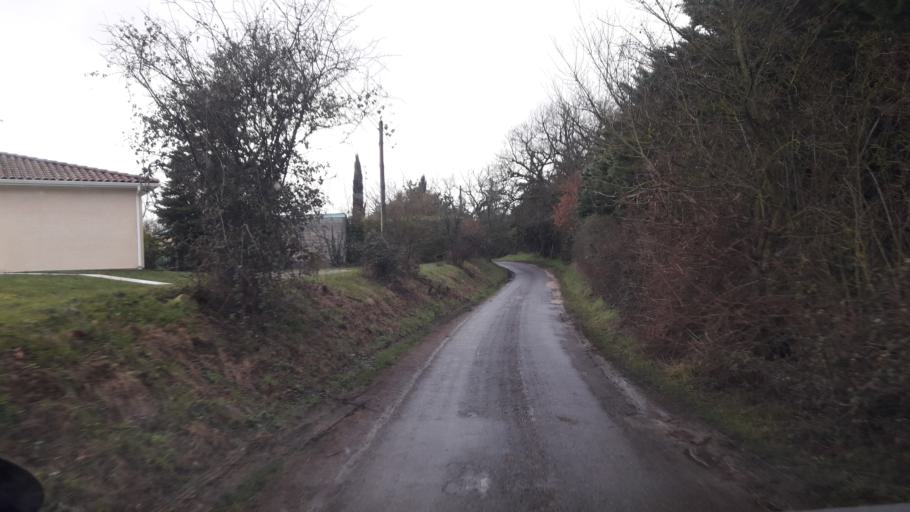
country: FR
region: Midi-Pyrenees
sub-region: Departement de la Haute-Garonne
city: Carbonne
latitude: 43.2933
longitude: 1.2475
